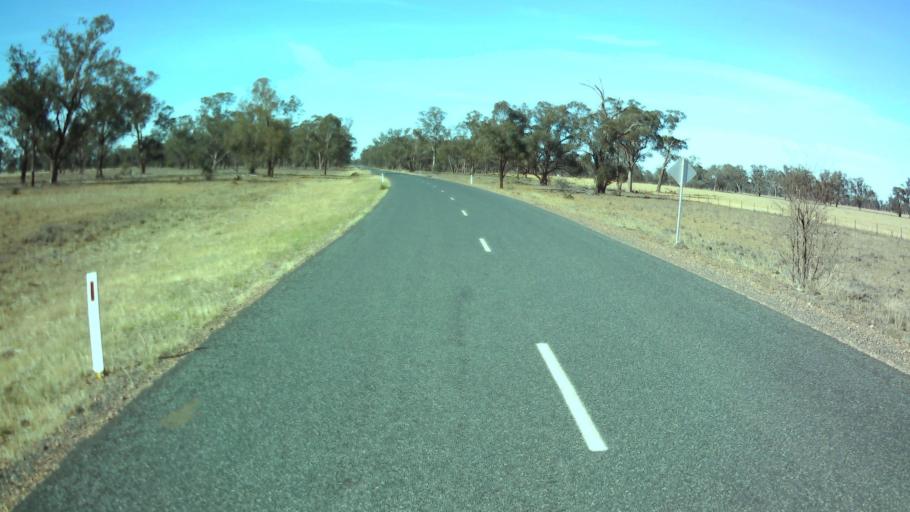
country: AU
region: New South Wales
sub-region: Weddin
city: Grenfell
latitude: -34.0594
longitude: 147.9113
